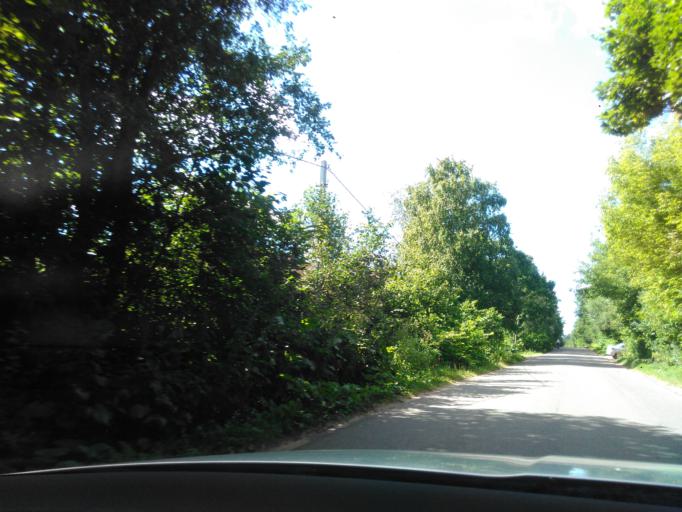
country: RU
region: Moskovskaya
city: Klin
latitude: 56.2298
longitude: 36.8149
